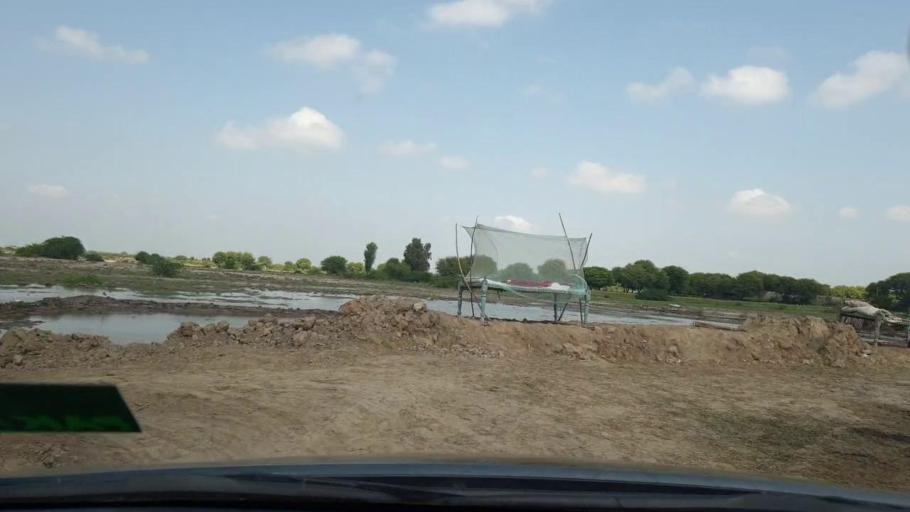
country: PK
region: Sindh
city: Tando Bago
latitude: 24.9564
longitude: 69.0752
